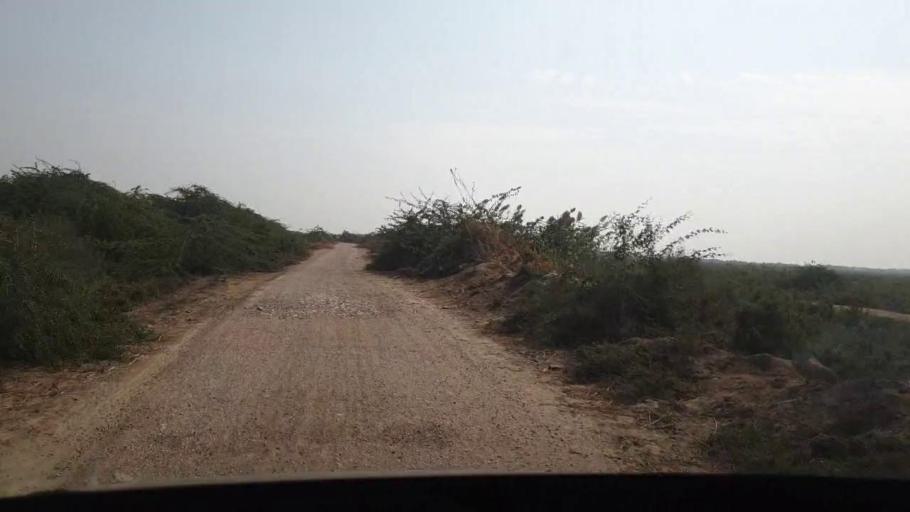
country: PK
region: Sindh
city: Chuhar Jamali
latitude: 24.2502
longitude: 67.9894
